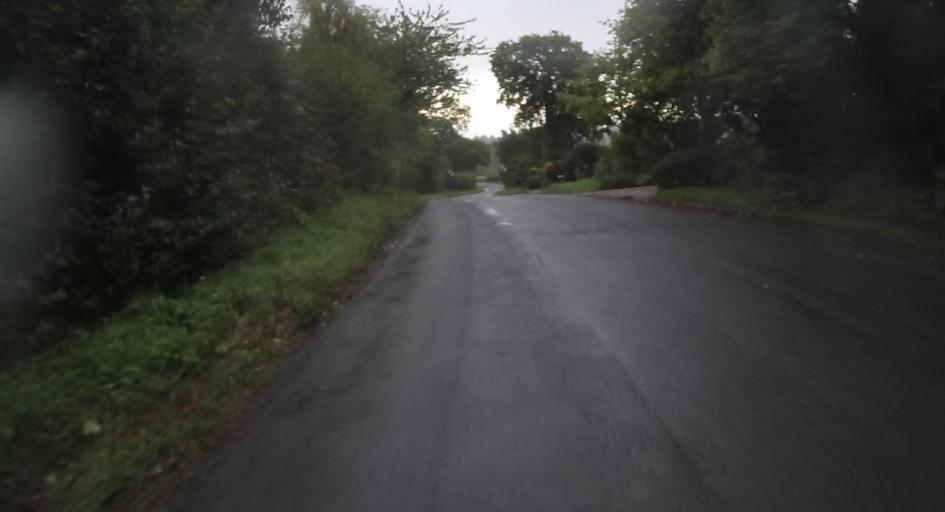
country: GB
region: England
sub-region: Hampshire
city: Tadley
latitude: 51.3142
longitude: -1.1450
